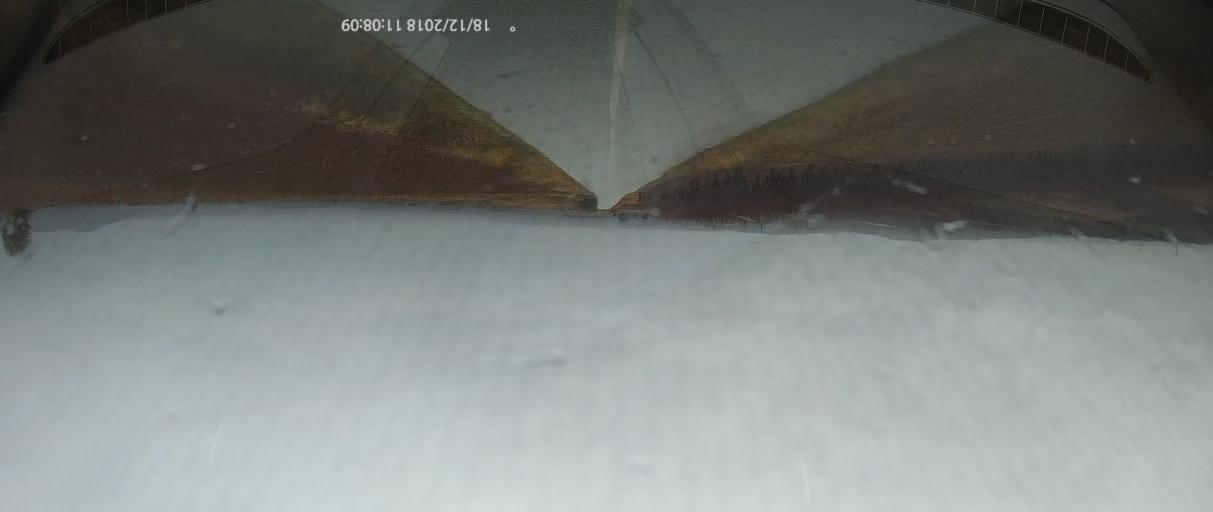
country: GR
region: Central Macedonia
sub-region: Nomos Pierias
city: Kato Milia
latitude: 40.2259
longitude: 22.3438
